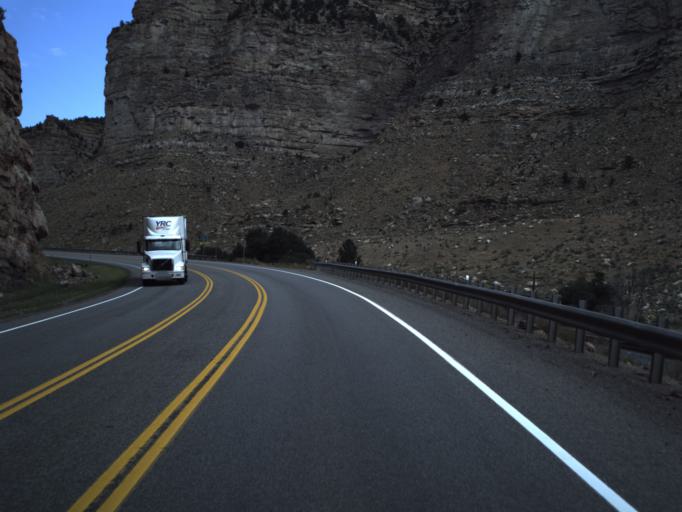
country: US
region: Utah
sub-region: Carbon County
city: Helper
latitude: 39.7388
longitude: -110.8746
